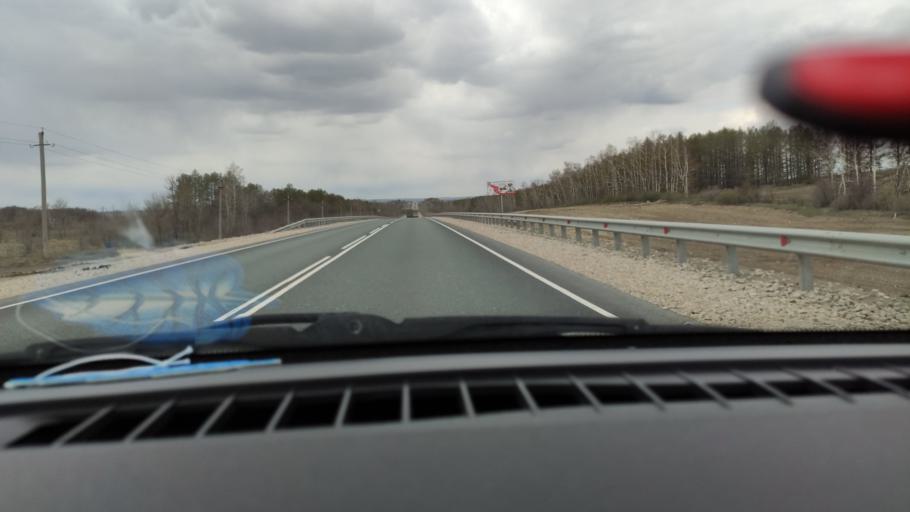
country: RU
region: Saratov
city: Shikhany
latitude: 52.1612
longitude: 47.1460
